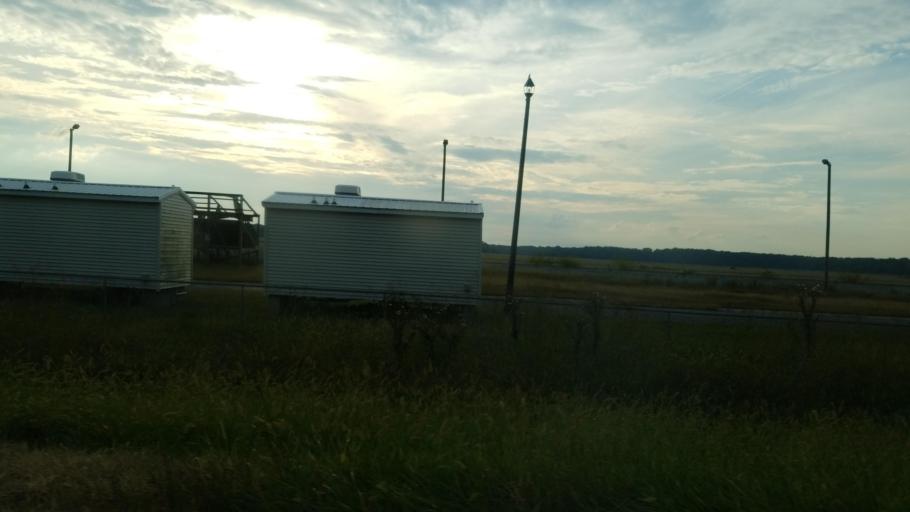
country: US
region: Illinois
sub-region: Saline County
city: Harrisburg
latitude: 37.7586
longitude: -88.5402
